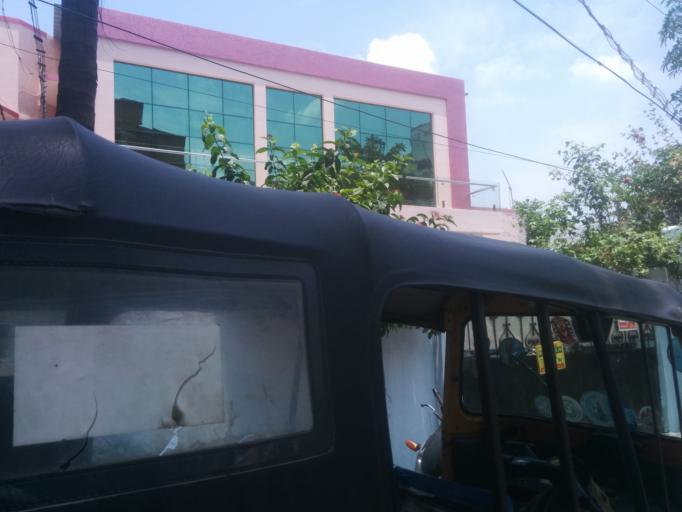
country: IN
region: Andhra Pradesh
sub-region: East Godavari
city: Rajahmundry
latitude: 17.0110
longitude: 81.7713
